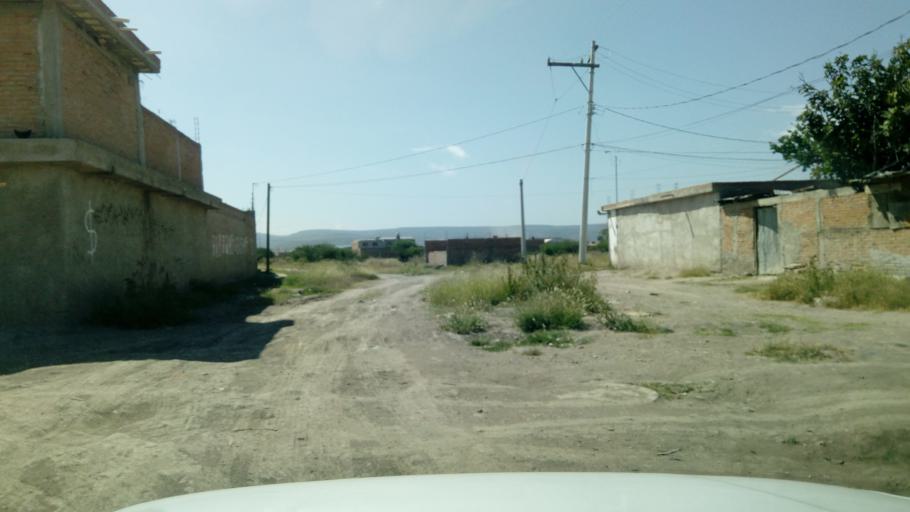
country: MX
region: Durango
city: Victoria de Durango
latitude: 23.9860
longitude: -104.6698
